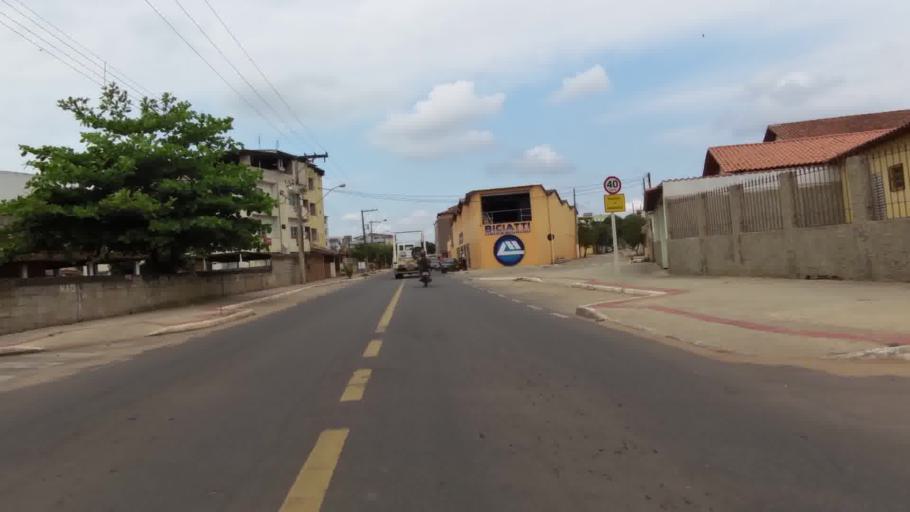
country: BR
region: Espirito Santo
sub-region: Piuma
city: Piuma
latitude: -20.8461
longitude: -40.7461
